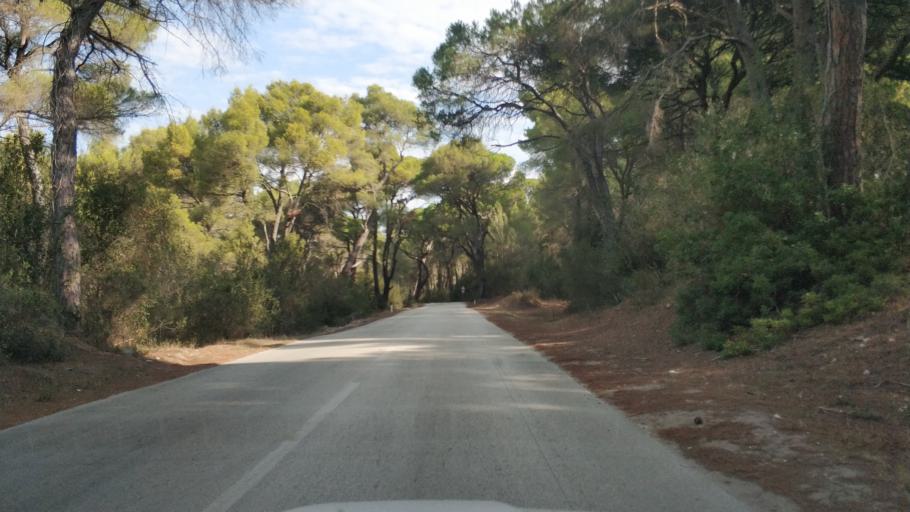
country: AL
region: Fier
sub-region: Rrethi i Lushnjes
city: Divjake
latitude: 40.9841
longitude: 19.4827
